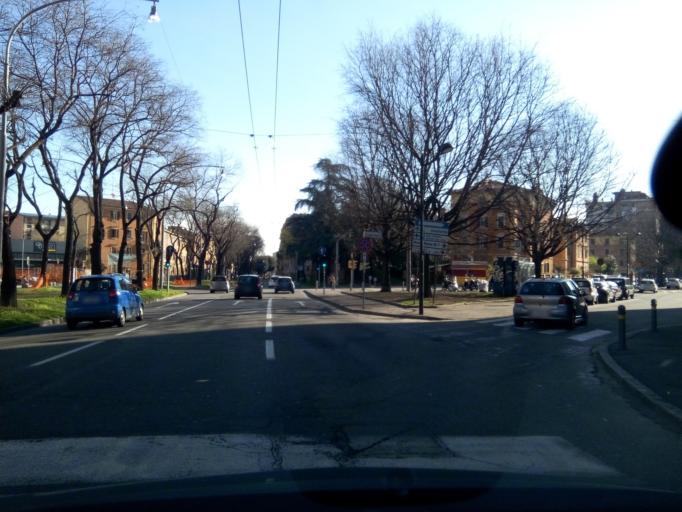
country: IT
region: Emilia-Romagna
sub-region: Provincia di Bologna
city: Bologna
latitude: 44.5006
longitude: 11.3296
